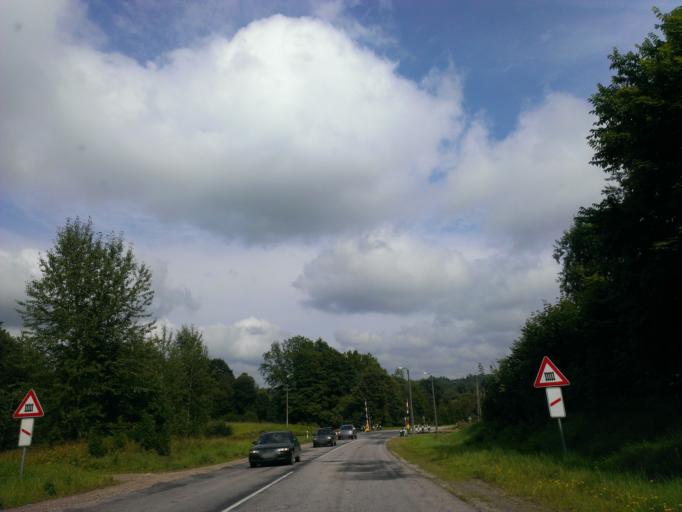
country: LV
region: Amatas Novads
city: Drabesi
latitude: 57.2413
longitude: 25.3020
